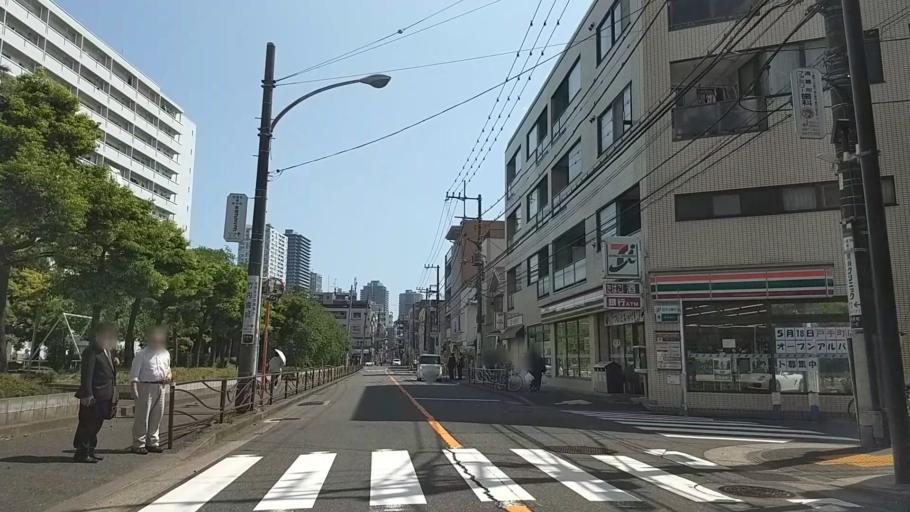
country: JP
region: Kanagawa
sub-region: Kawasaki-shi
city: Kawasaki
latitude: 35.5396
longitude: 139.6914
